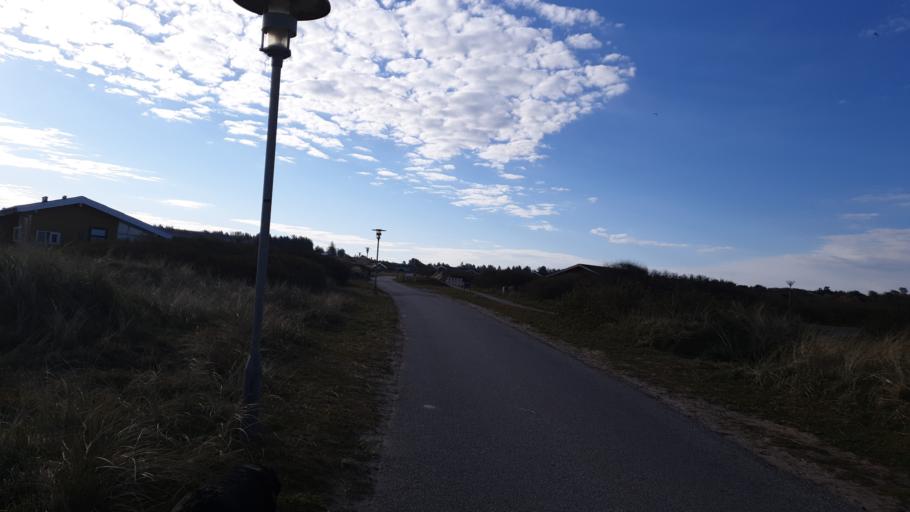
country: DK
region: North Denmark
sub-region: Hjorring Kommune
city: Hjorring
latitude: 57.4918
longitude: 9.8302
